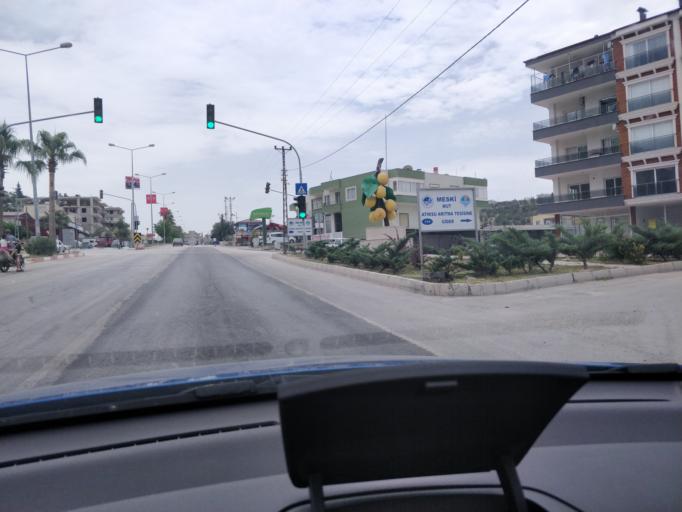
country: TR
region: Mersin
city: Mut
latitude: 36.6504
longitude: 33.4257
